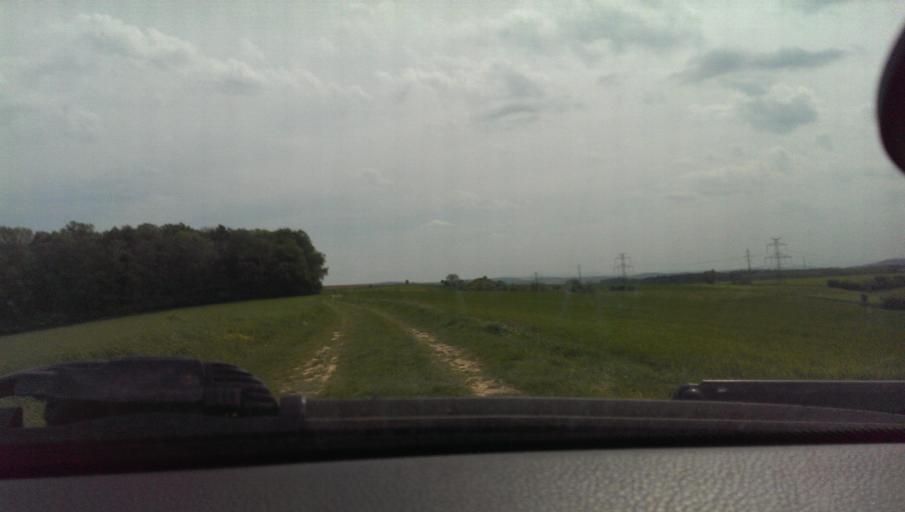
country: CZ
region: Zlin
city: Tlumacov
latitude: 49.2613
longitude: 17.5322
